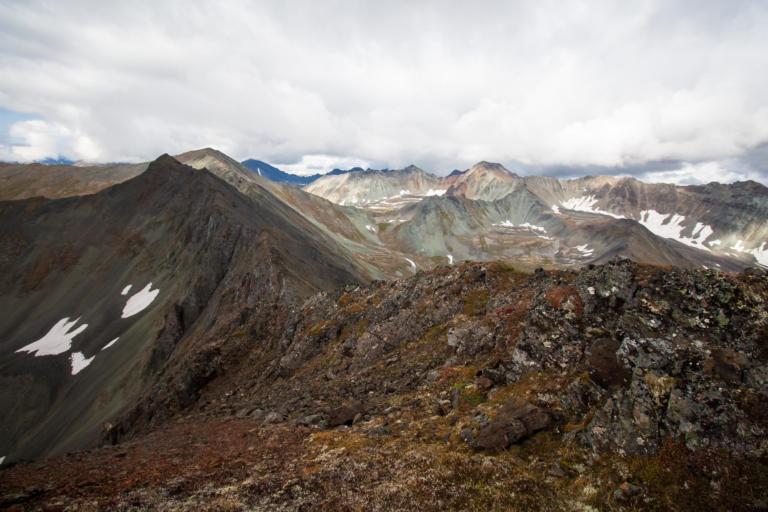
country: RU
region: Kamtsjatka
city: Yelizovo
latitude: 53.8447
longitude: 158.1889
